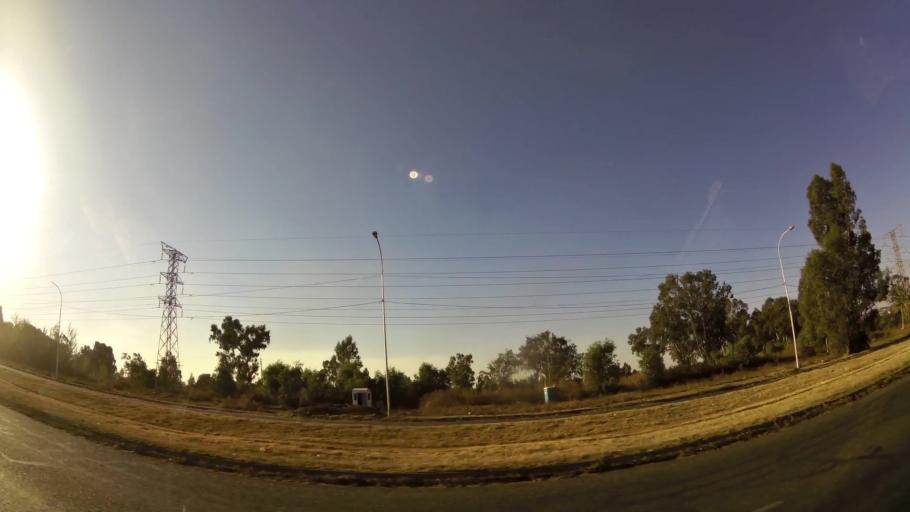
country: ZA
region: Gauteng
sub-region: City of Johannesburg Metropolitan Municipality
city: Roodepoort
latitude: -26.1998
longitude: 27.9413
